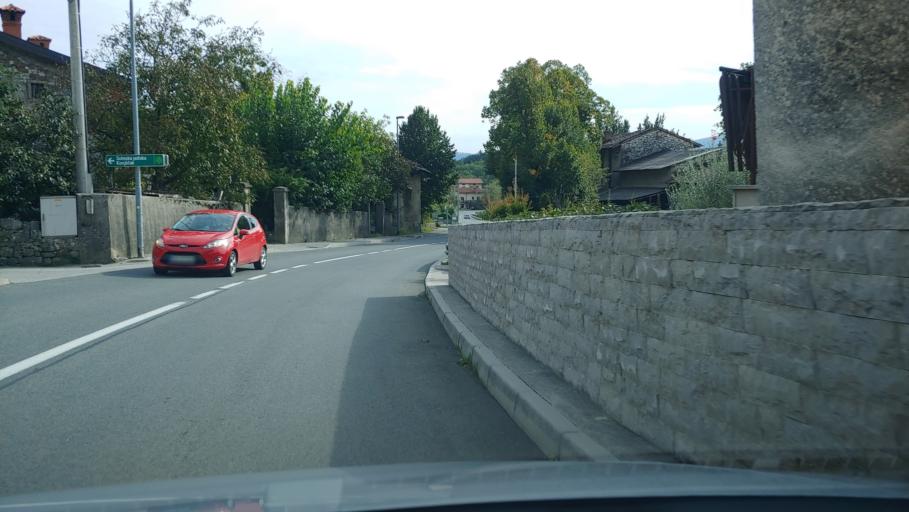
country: SI
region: Nova Gorica
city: Sempas
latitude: 45.9073
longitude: 13.7798
